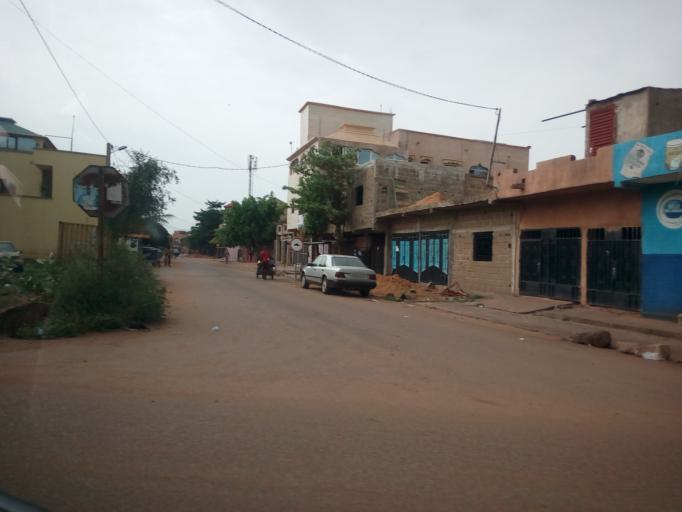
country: ML
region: Bamako
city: Bamako
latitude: 12.6208
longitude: -8.0368
